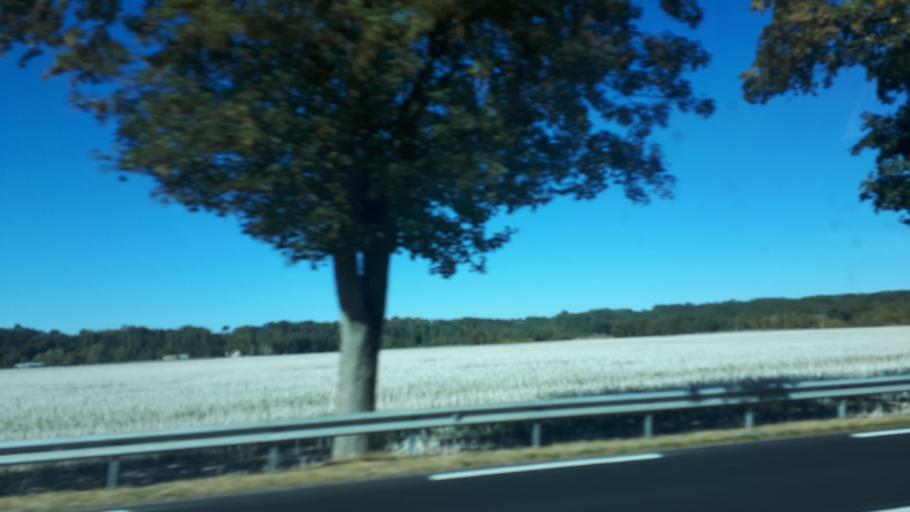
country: FR
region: Centre
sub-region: Departement d'Eure-et-Loir
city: Marboue
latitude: 48.1045
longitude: 1.3300
